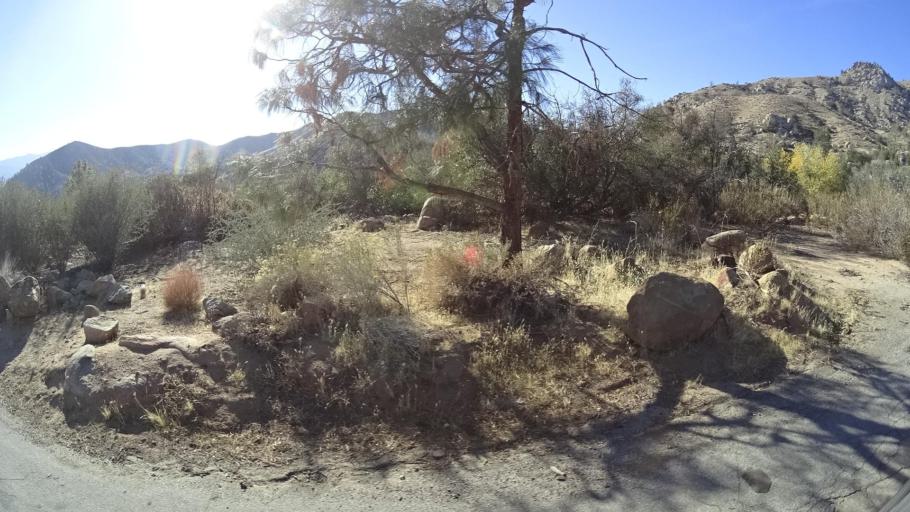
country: US
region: California
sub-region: Kern County
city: Weldon
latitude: 35.7137
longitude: -118.3052
